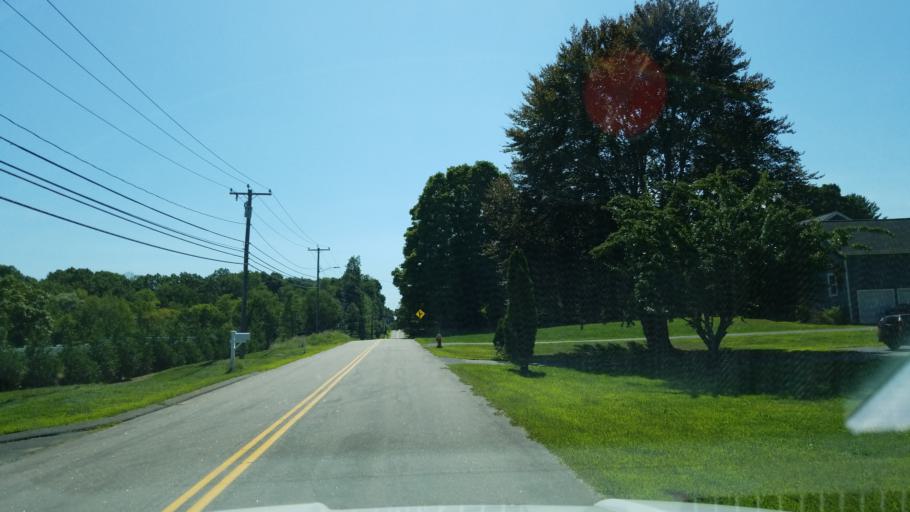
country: US
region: Connecticut
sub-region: Hartford County
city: Tariffville
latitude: 41.8559
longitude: -72.7579
